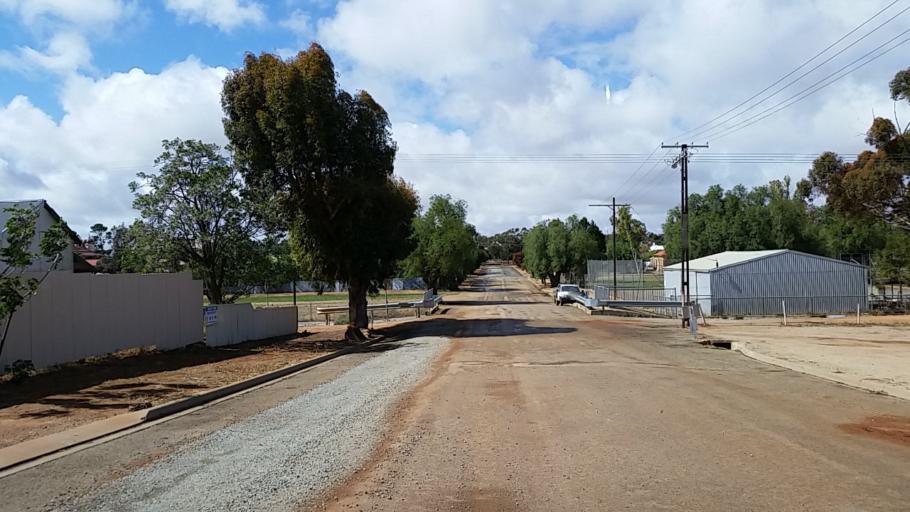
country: AU
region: South Australia
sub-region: Peterborough
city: Peterborough
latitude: -32.9711
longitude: 138.8331
